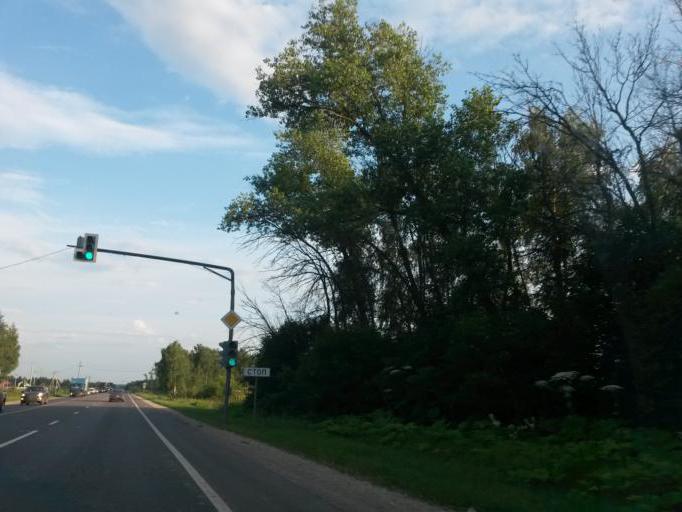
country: RU
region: Moskovskaya
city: Belyye Stolby
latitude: 55.2773
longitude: 37.8249
